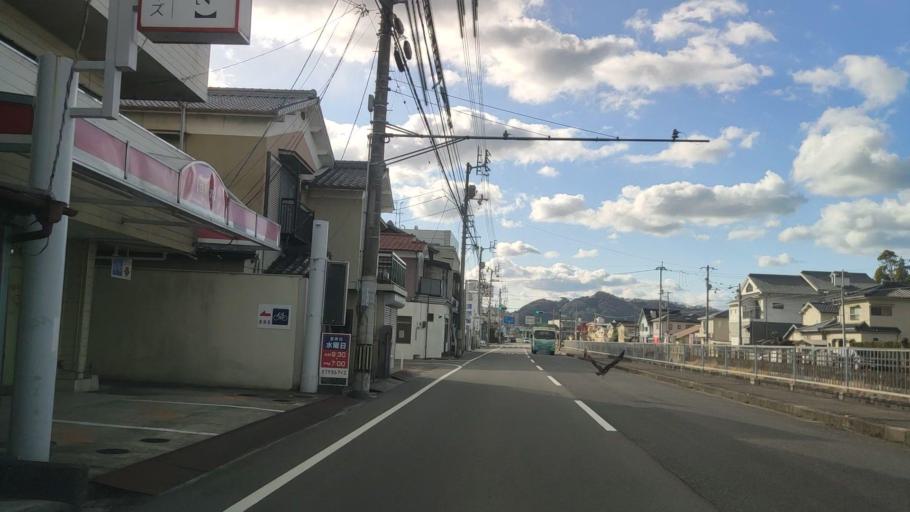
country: JP
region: Ehime
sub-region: Shikoku-chuo Shi
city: Matsuyama
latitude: 33.8613
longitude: 132.7196
